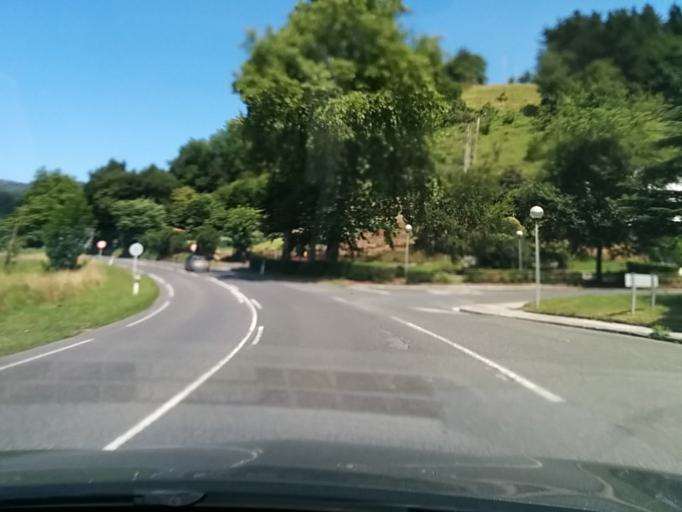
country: ES
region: Basque Country
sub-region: Provincia de Guipuzcoa
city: Usurbil
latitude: 43.2731
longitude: -2.0538
